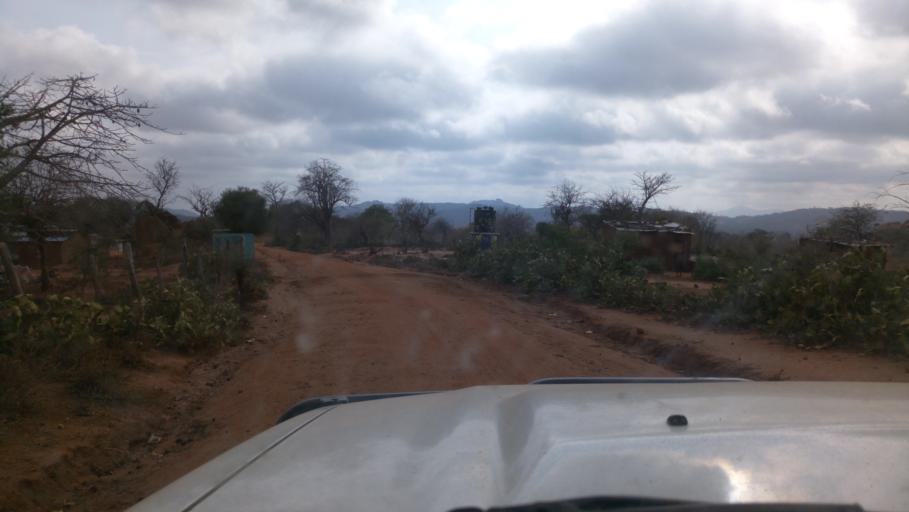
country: KE
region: Kitui
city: Kitui
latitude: -1.8558
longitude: 38.2479
